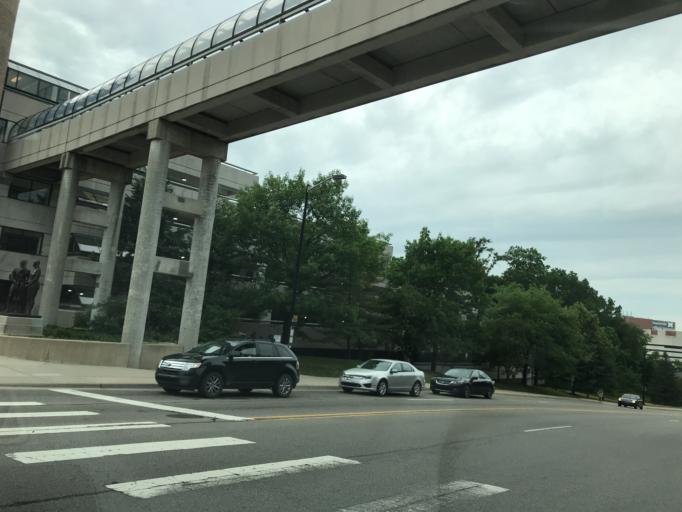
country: US
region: Michigan
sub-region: Washtenaw County
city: Ann Arbor
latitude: 42.2832
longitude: -83.7356
